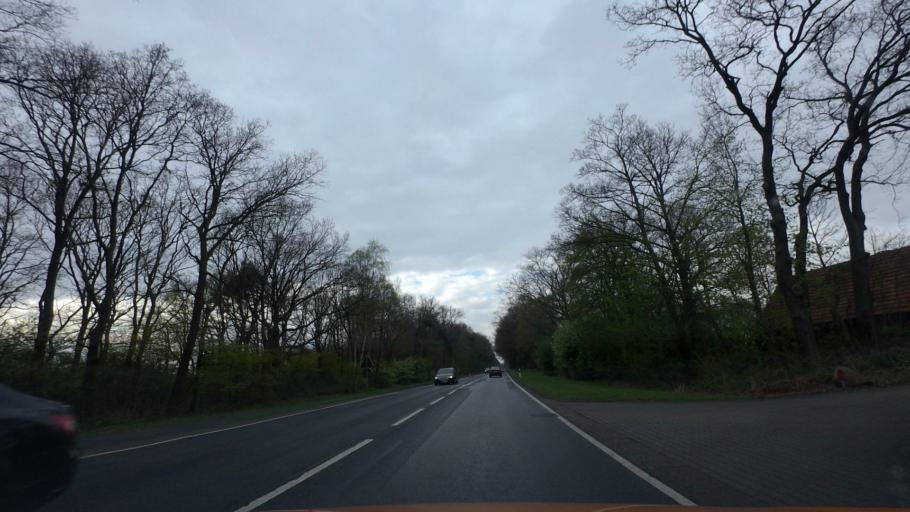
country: DE
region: Lower Saxony
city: Molbergen
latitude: 52.9201
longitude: 7.9541
